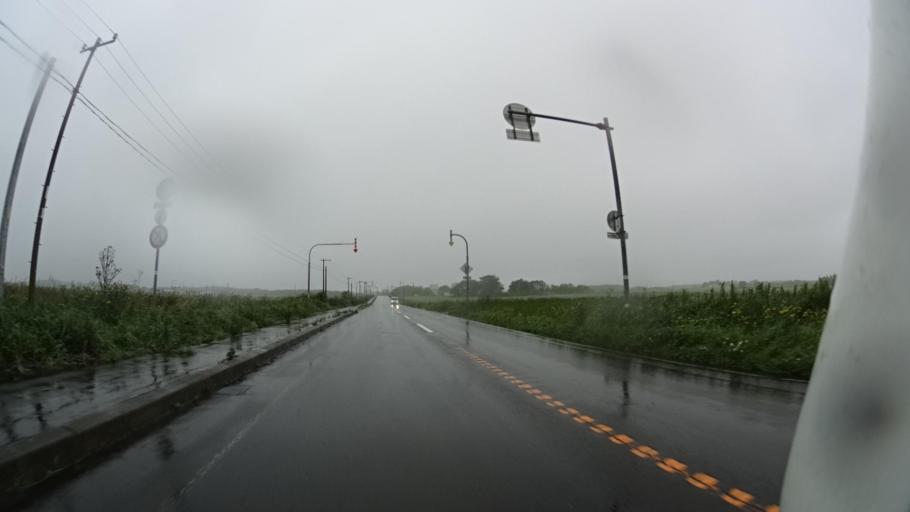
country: JP
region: Hokkaido
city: Nemuro
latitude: 43.2777
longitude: 145.5235
